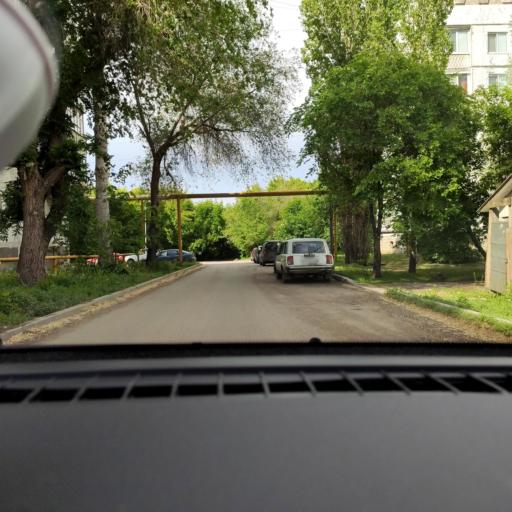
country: RU
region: Samara
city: Samara
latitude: 53.1369
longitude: 50.1578
